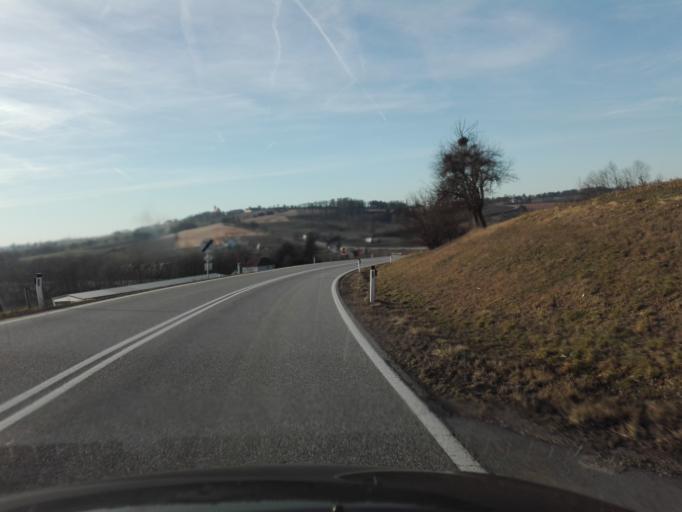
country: AT
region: Lower Austria
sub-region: Politischer Bezirk Amstetten
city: Strengberg
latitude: 48.1376
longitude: 14.6769
